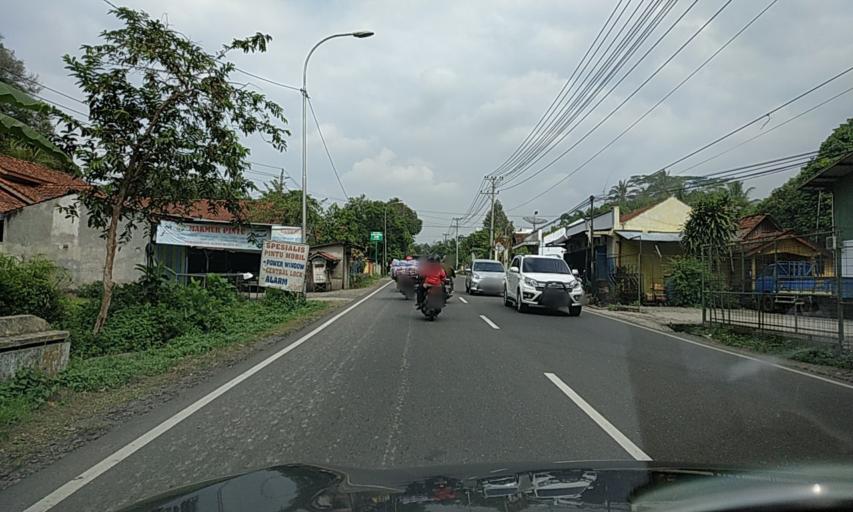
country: ID
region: Central Java
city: Purwokerto
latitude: -7.4162
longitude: 109.1805
